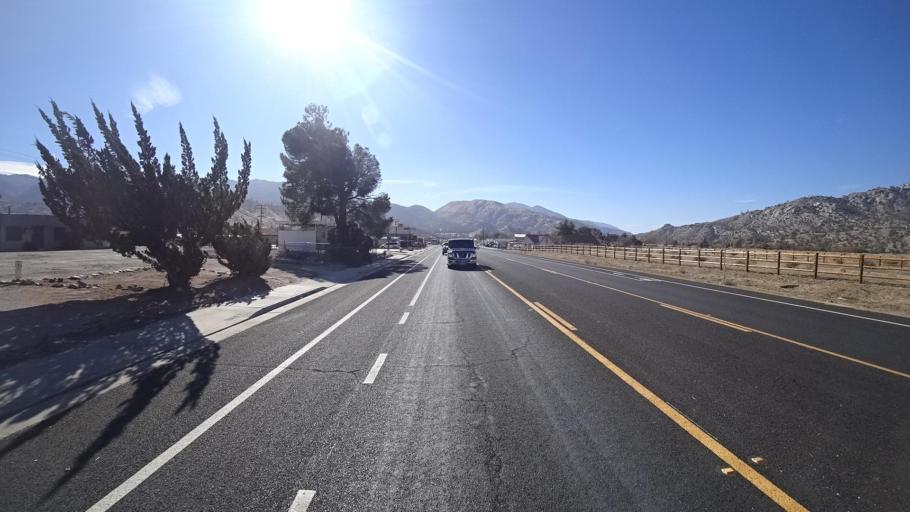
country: US
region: California
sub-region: Kern County
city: Lake Isabella
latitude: 35.6140
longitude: -118.4800
